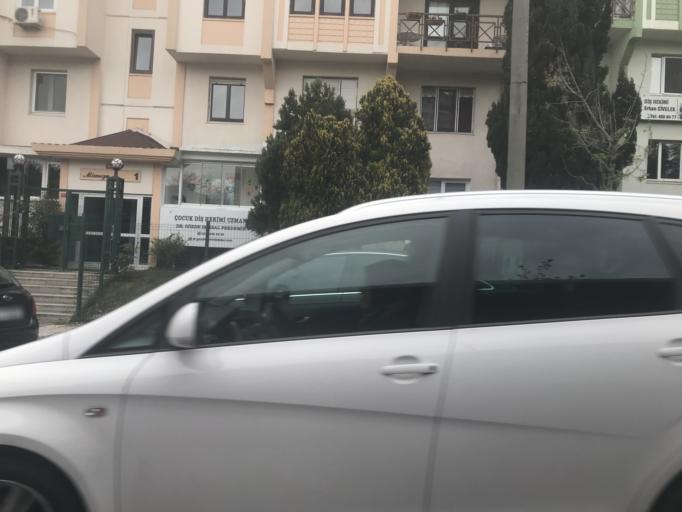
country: TR
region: Istanbul
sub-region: Atasehir
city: Atasehir
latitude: 40.9914
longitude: 29.1327
